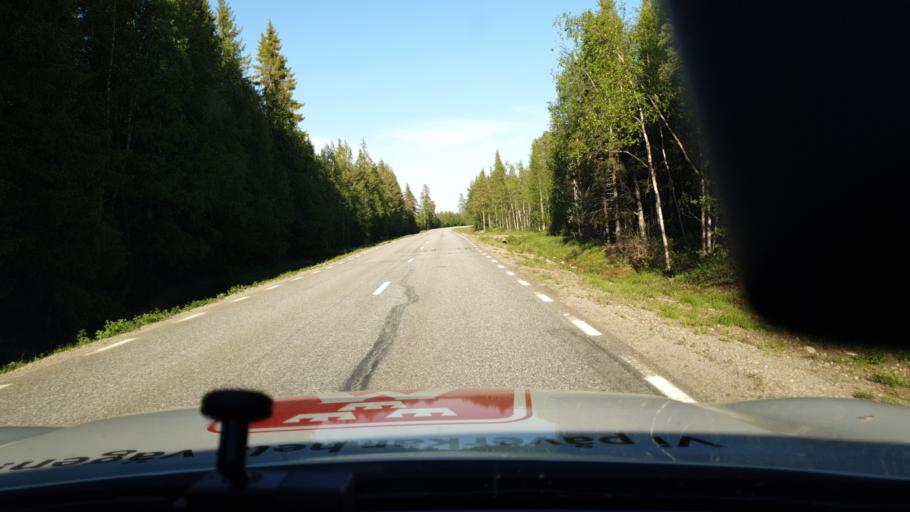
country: SE
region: Vaesterbotten
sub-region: Lycksele Kommun
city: Soderfors
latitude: 64.6334
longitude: 17.9688
